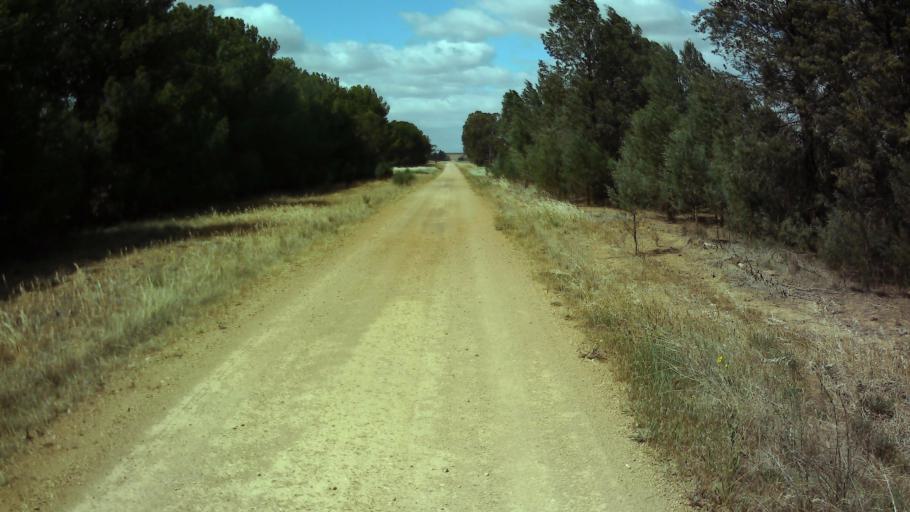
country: AU
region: New South Wales
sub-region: Weddin
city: Grenfell
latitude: -34.0480
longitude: 148.3326
